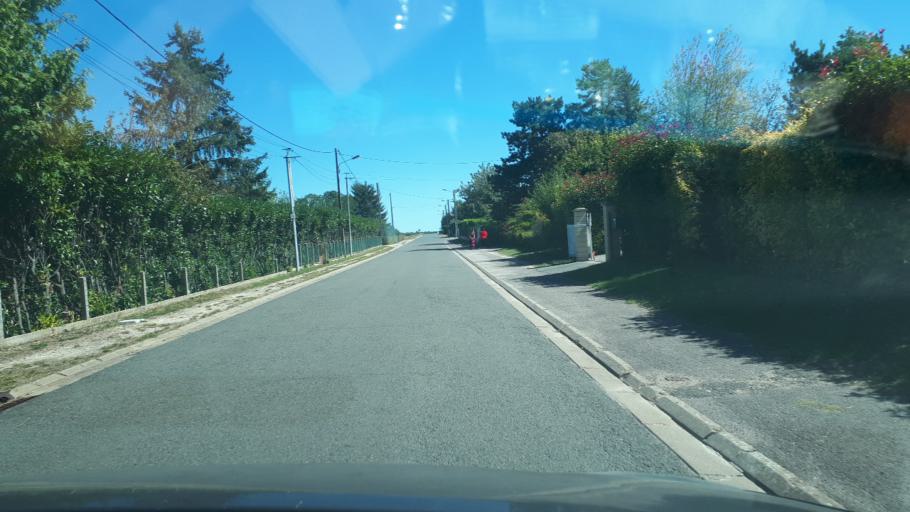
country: FR
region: Centre
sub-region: Departement du Cher
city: Rians
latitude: 47.1861
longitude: 2.6189
